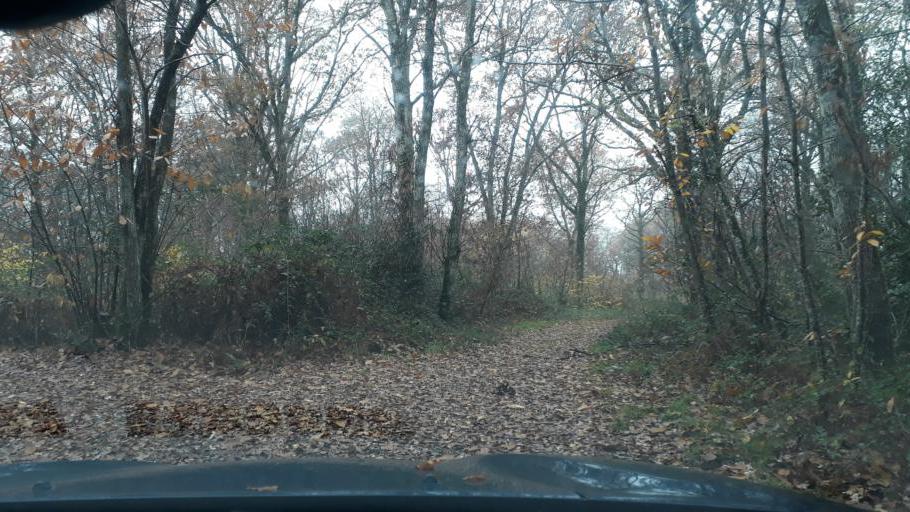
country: FR
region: Centre
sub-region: Departement du Loiret
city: Menestreau-en-Villette
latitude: 47.7240
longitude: 2.0059
